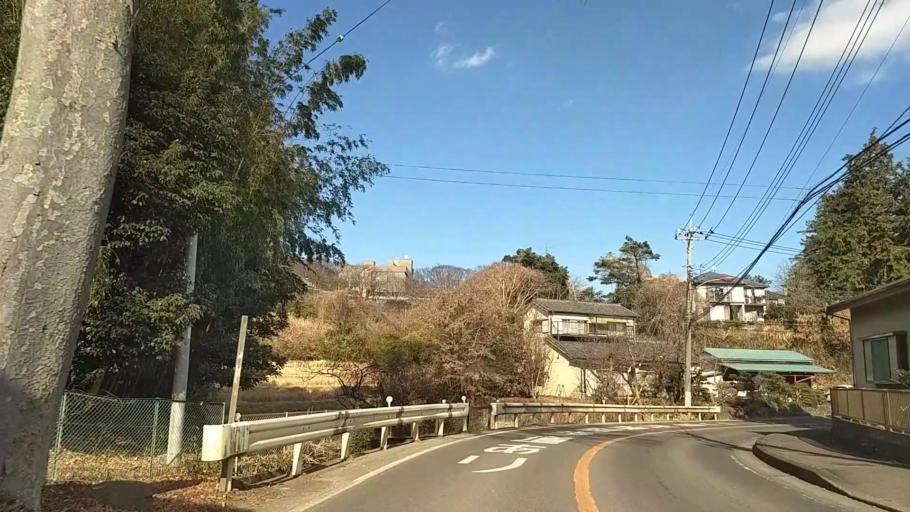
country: JP
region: Kanagawa
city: Isehara
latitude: 35.4201
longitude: 139.2898
